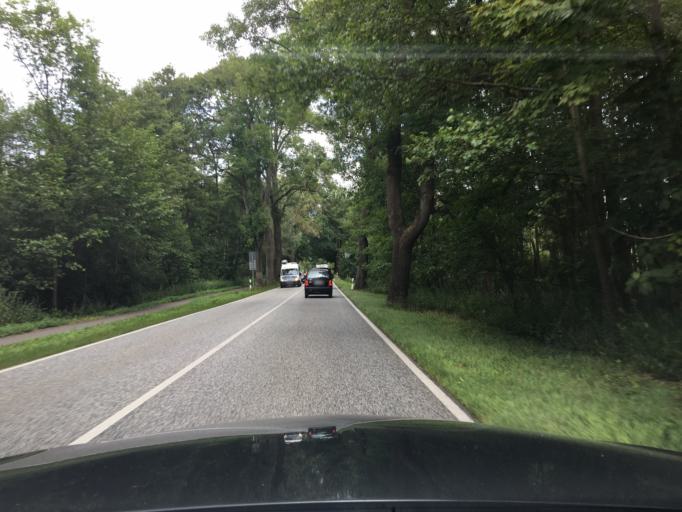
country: DE
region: Brandenburg
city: Gransee
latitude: 53.0733
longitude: 13.1815
